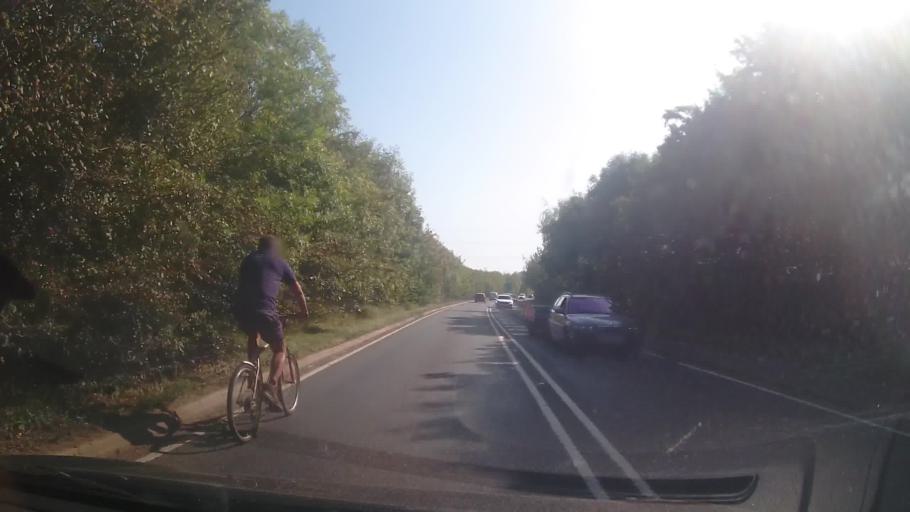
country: GB
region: England
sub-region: Worcestershire
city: Evesham
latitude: 52.1152
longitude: -1.9652
